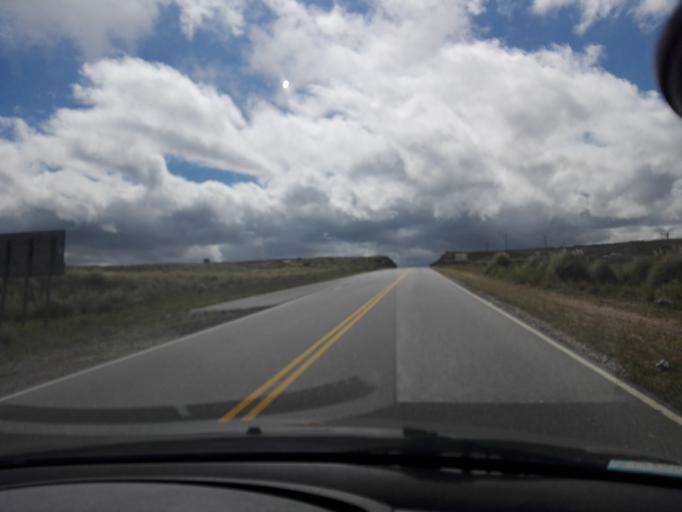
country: AR
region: Cordoba
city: Mina Clavero
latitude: -31.6109
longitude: -64.8249
